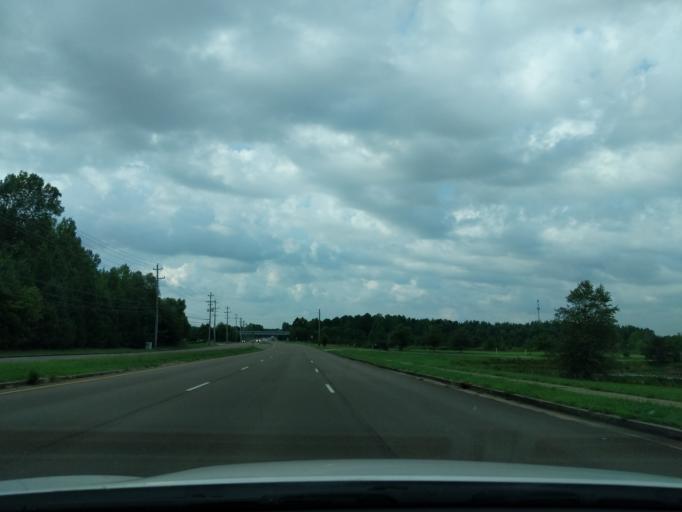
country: US
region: Tennessee
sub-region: Shelby County
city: Germantown
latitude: 35.0326
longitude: -89.7600
